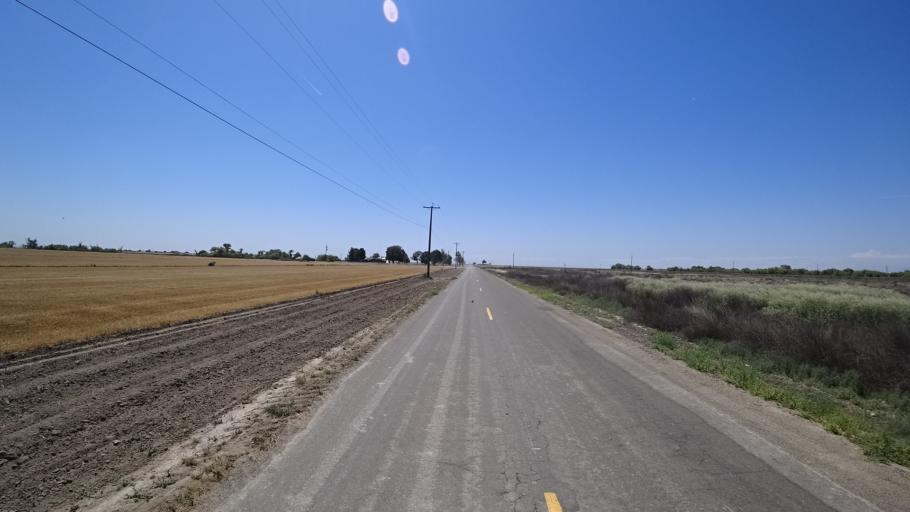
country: US
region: California
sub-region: Kings County
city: Armona
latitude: 36.2349
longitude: -119.7267
